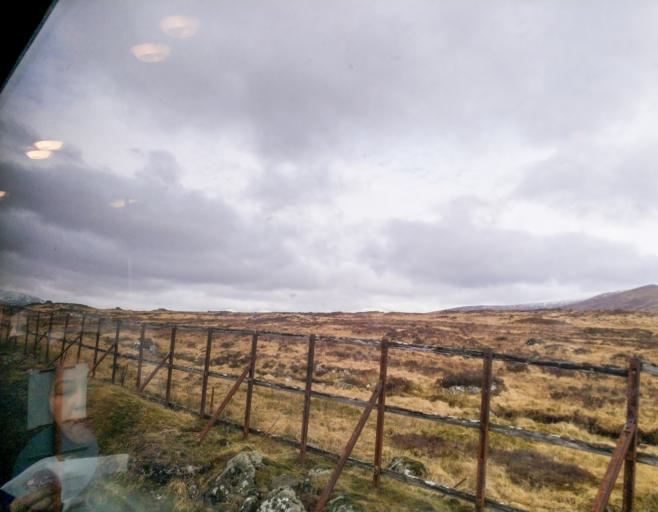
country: GB
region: Scotland
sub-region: Highland
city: Spean Bridge
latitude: 56.7018
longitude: -4.5787
